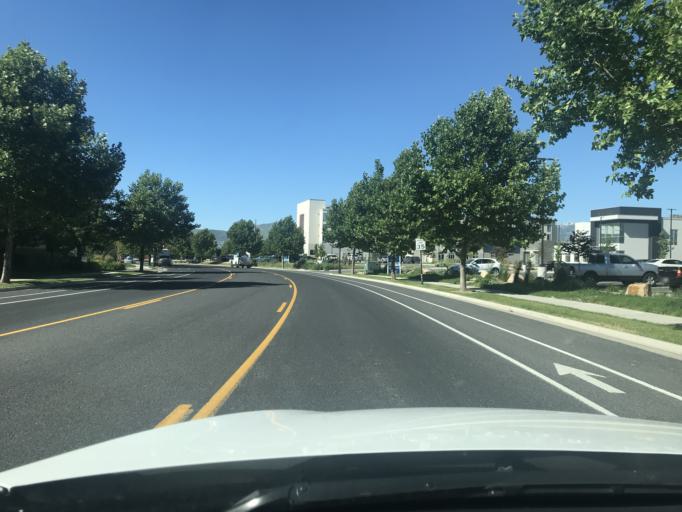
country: US
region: Utah
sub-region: Salt Lake County
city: South Jordan Heights
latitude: 40.5476
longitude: -111.9813
